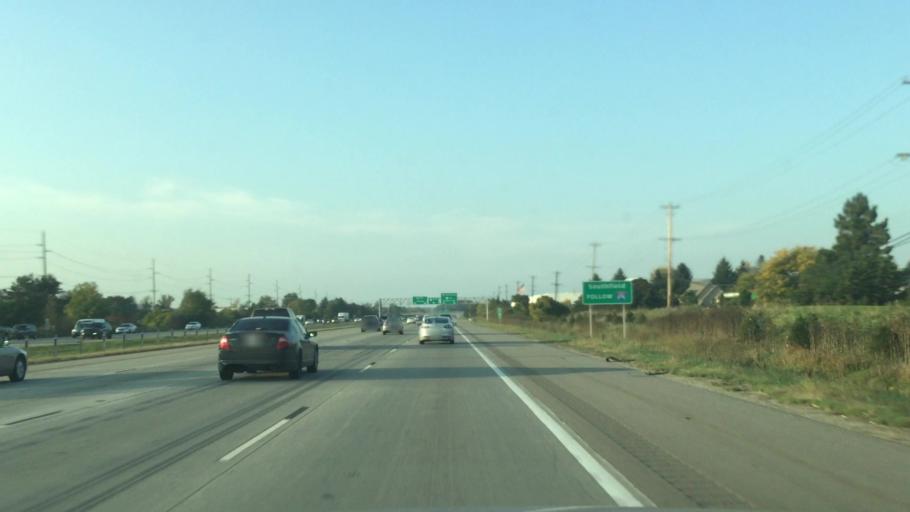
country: US
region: Michigan
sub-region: Oakland County
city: Novi
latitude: 42.4549
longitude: -83.4311
